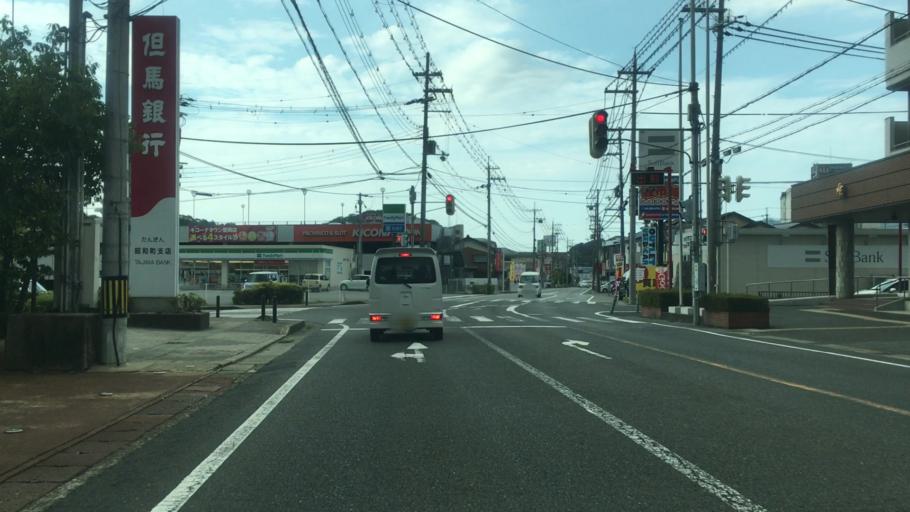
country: JP
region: Hyogo
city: Toyooka
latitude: 35.5309
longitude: 134.8198
